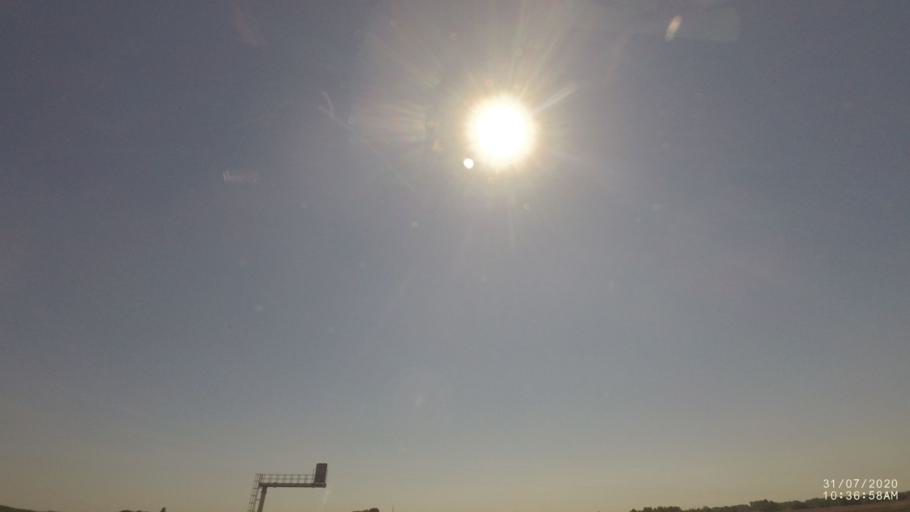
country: SK
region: Trnavsky
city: Dunajska Streda
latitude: 48.0101
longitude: 17.4645
